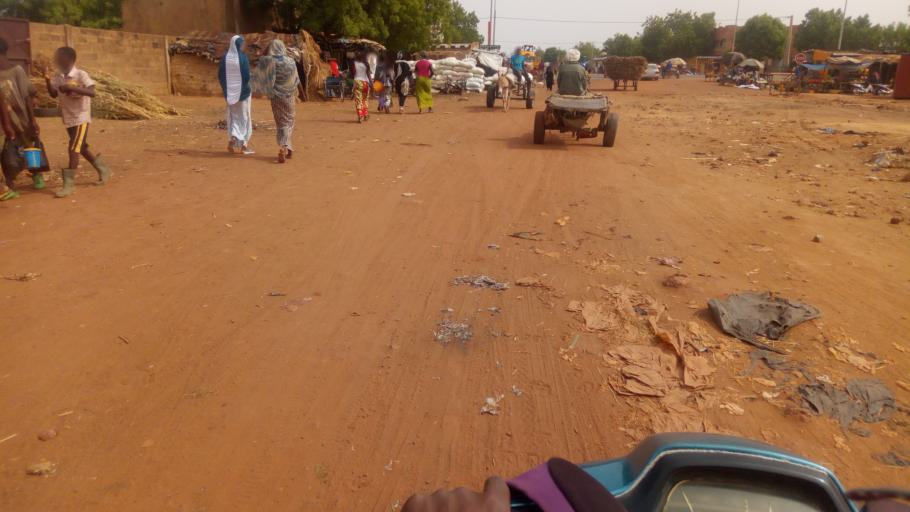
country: ML
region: Segou
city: Segou
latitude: 13.4303
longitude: -6.2612
